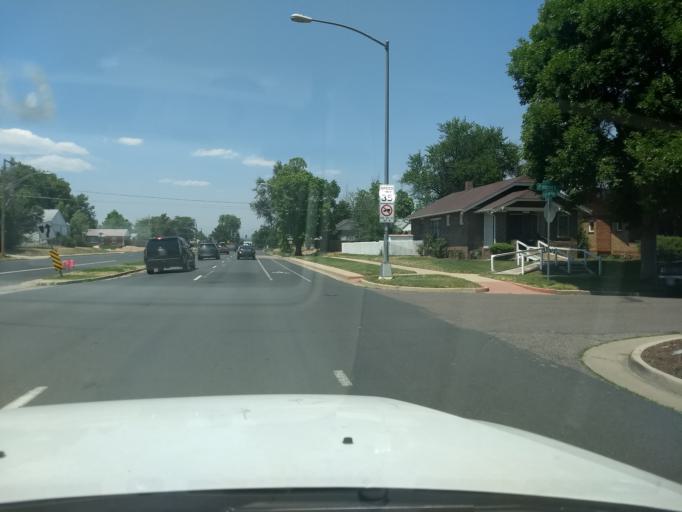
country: US
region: Colorado
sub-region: Denver County
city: Denver
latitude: 39.7620
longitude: -104.9535
